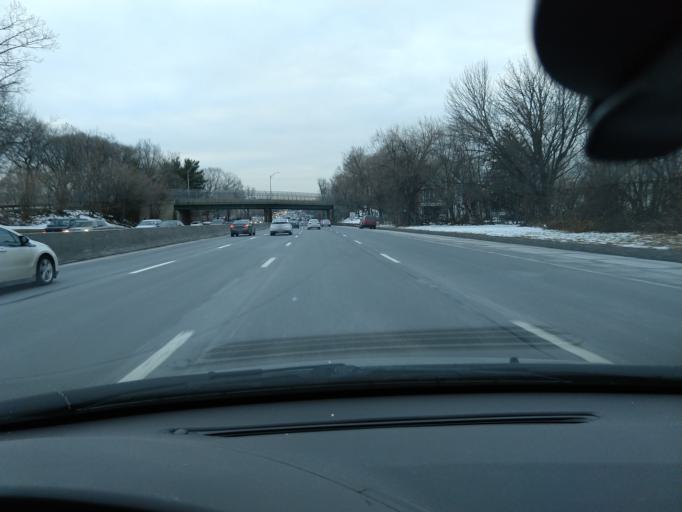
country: US
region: New Jersey
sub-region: Essex County
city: East Orange
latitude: 40.7504
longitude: -74.2123
